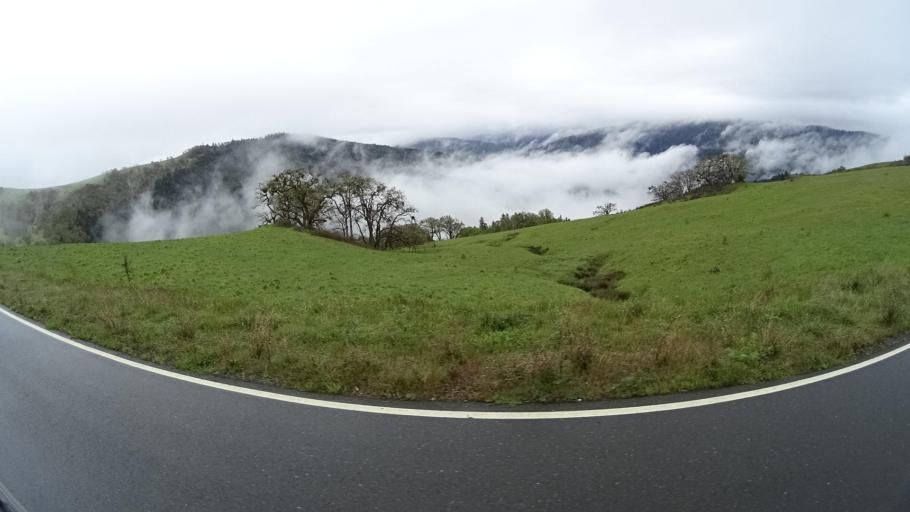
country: US
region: California
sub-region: Humboldt County
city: Westhaven-Moonstone
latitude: 41.1627
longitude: -123.9010
